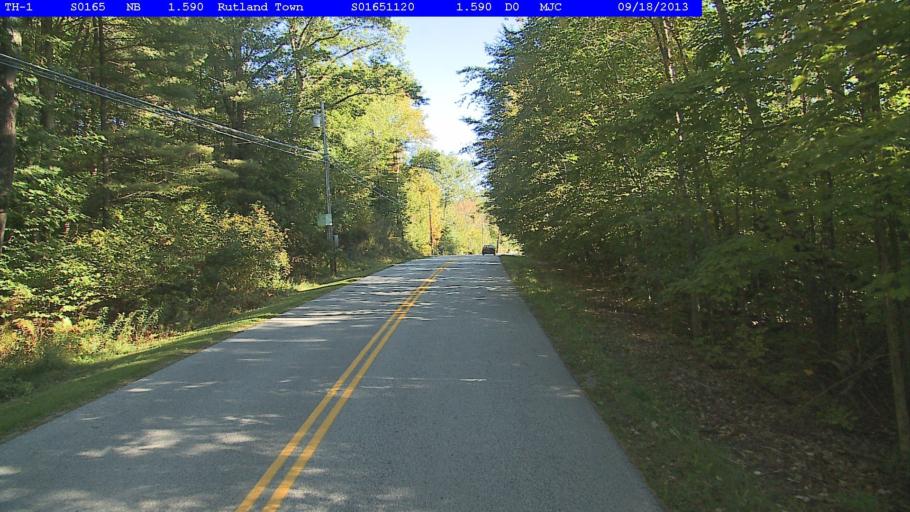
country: US
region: Vermont
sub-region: Rutland County
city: Rutland
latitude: 43.6625
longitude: -72.9497
